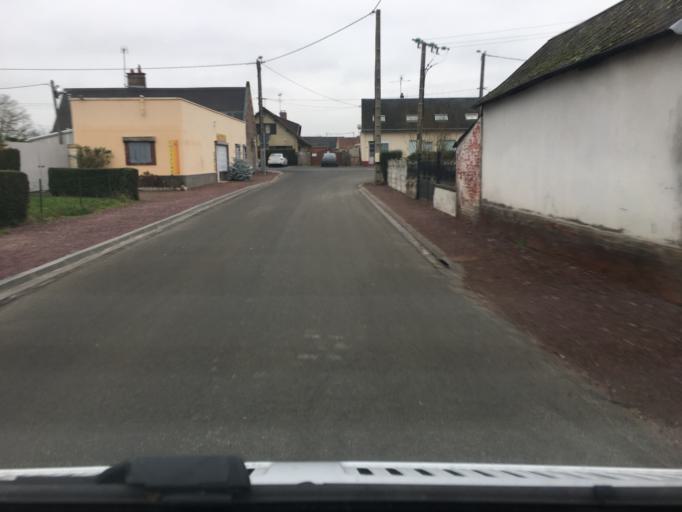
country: FR
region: Picardie
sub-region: Departement de la Somme
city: Pende
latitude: 50.1620
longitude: 1.5564
